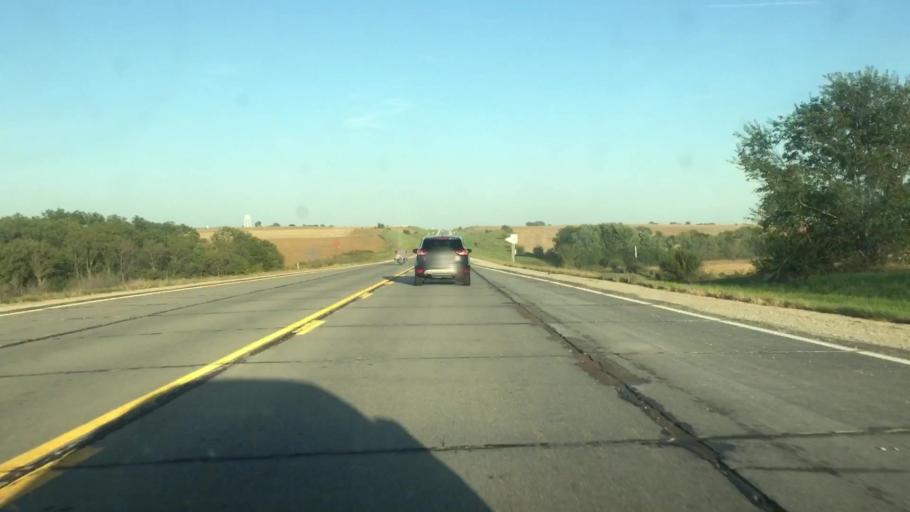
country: US
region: Kansas
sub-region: Atchison County
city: Atchison
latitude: 39.5568
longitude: -95.2712
